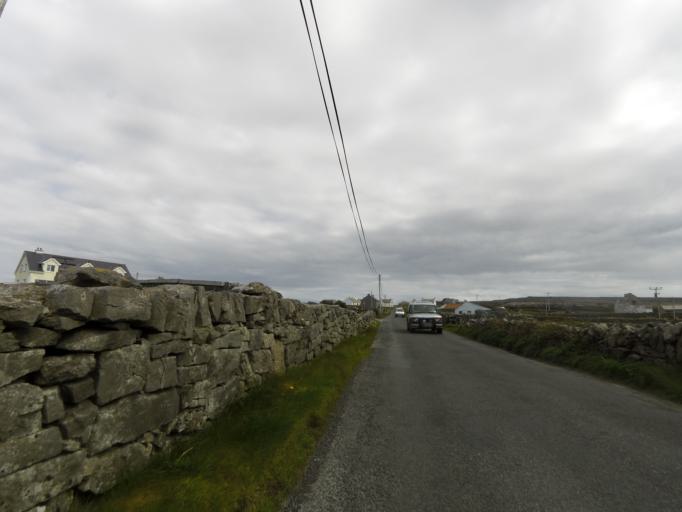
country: IE
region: Connaught
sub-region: County Galway
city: Clifden
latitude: 53.1307
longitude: -9.7392
